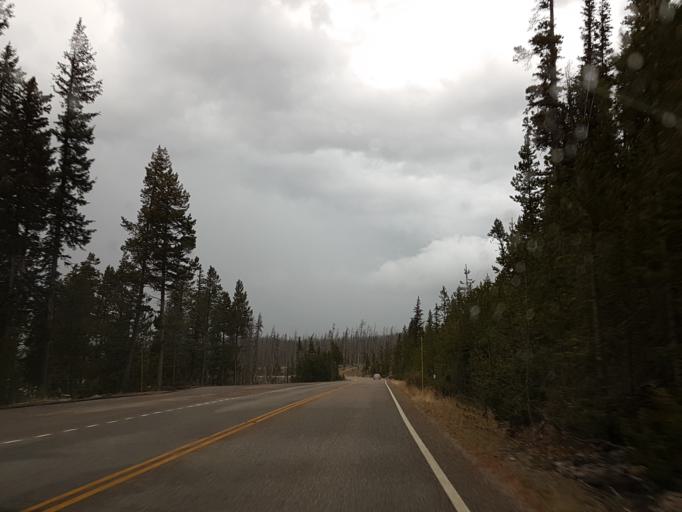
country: US
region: Montana
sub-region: Gallatin County
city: West Yellowstone
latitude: 44.4666
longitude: -110.5167
